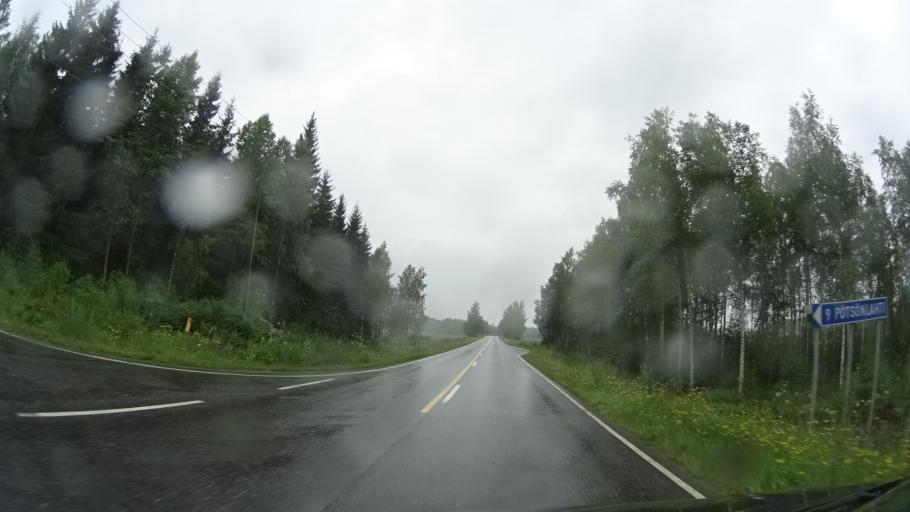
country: FI
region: North Karelia
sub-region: Keski-Karjala
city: Raeaekkylae
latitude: 62.3058
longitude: 29.5413
